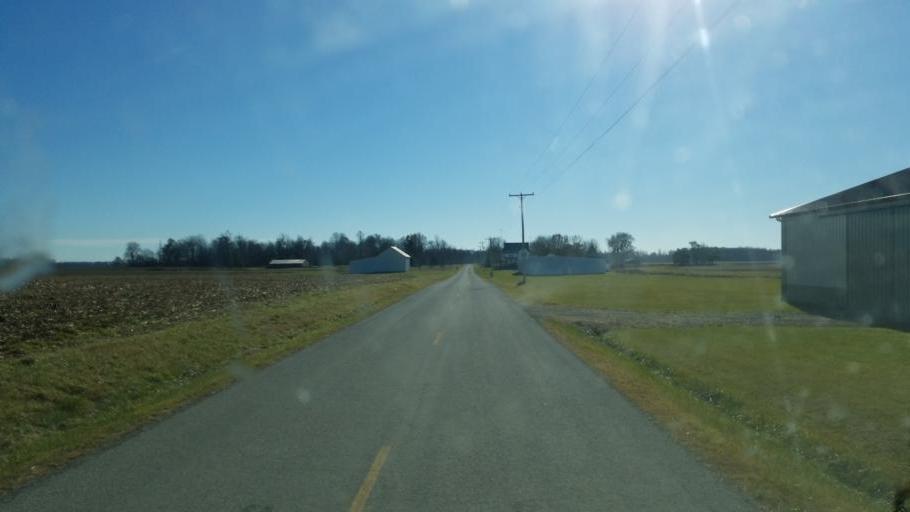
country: US
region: Ohio
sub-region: Crawford County
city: Galion
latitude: 40.8196
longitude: -82.8375
